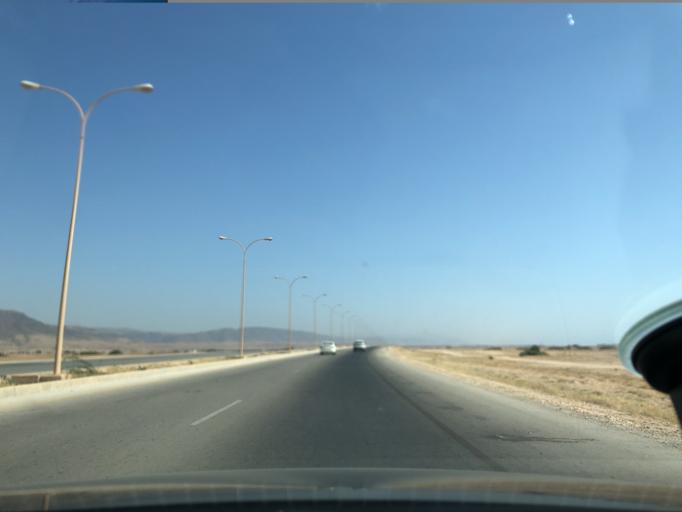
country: OM
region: Zufar
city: Salalah
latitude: 17.0505
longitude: 54.2522
